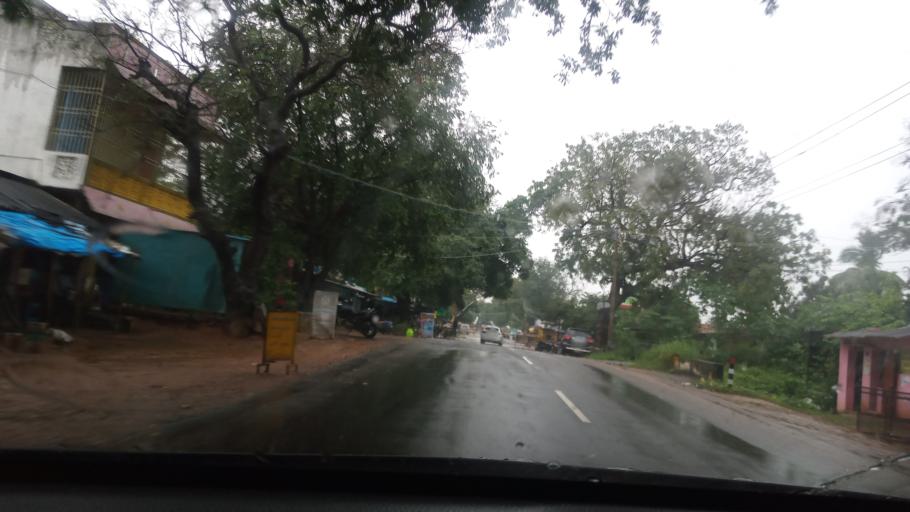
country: IN
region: Tamil Nadu
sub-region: Vellore
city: Kalavai
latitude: 12.8050
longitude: 79.4176
